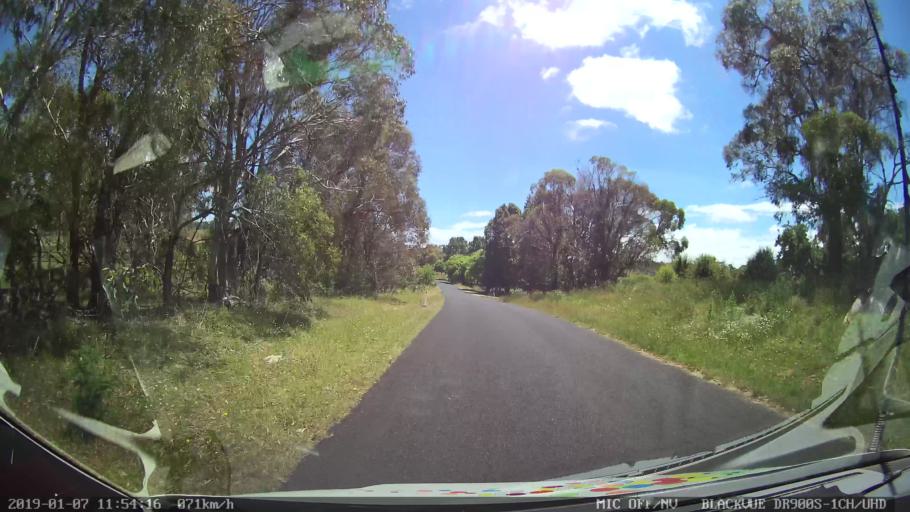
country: AU
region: New South Wales
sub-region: Guyra
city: Guyra
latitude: -30.2979
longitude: 151.6642
